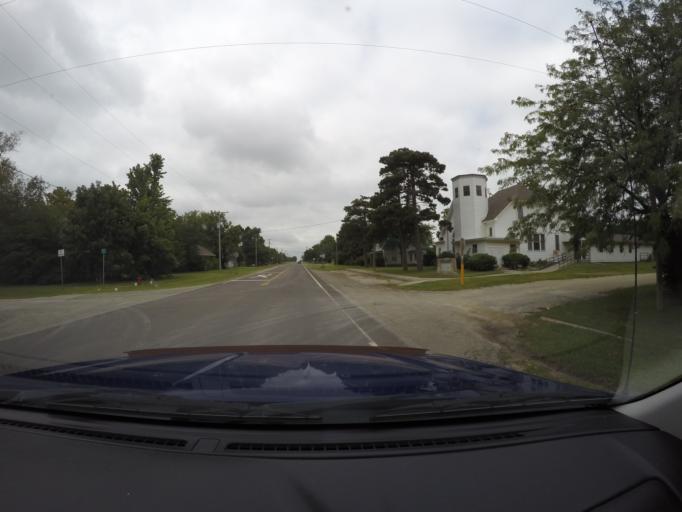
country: US
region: Kansas
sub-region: Morris County
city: Council Grove
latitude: 38.8448
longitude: -96.5940
